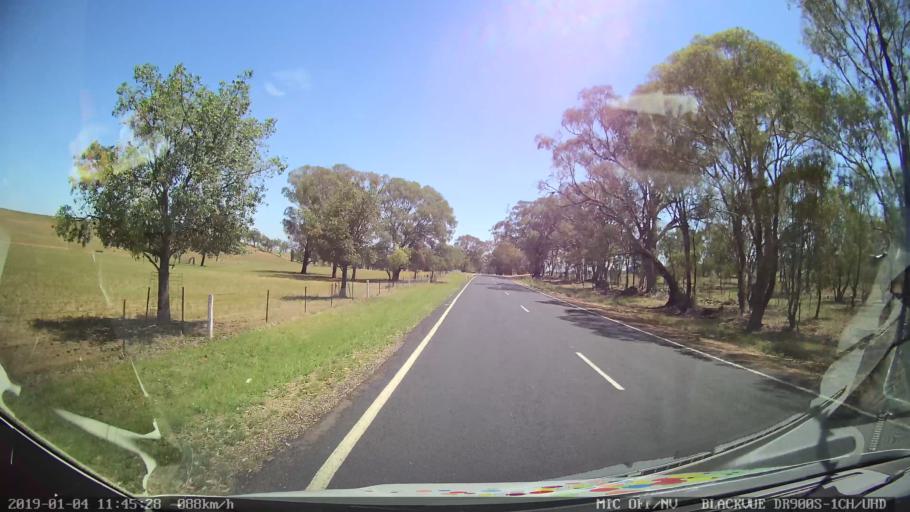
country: AU
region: New South Wales
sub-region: Cabonne
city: Molong
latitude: -32.9534
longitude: 148.7634
